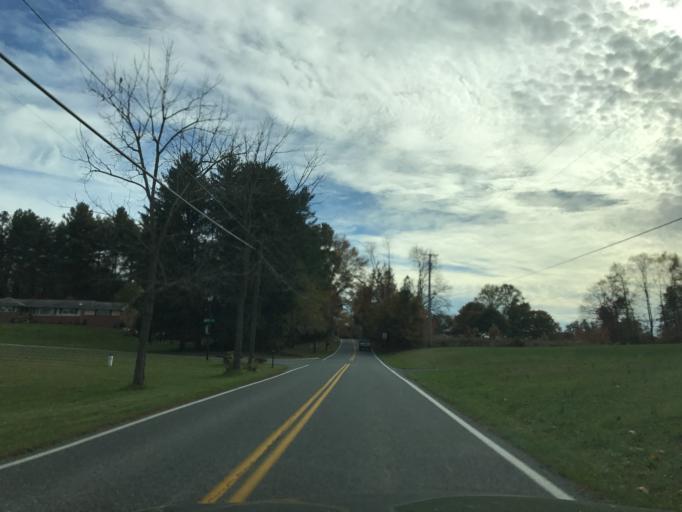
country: US
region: Maryland
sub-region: Harford County
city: Pleasant Hills
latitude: 39.4893
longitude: -76.3745
